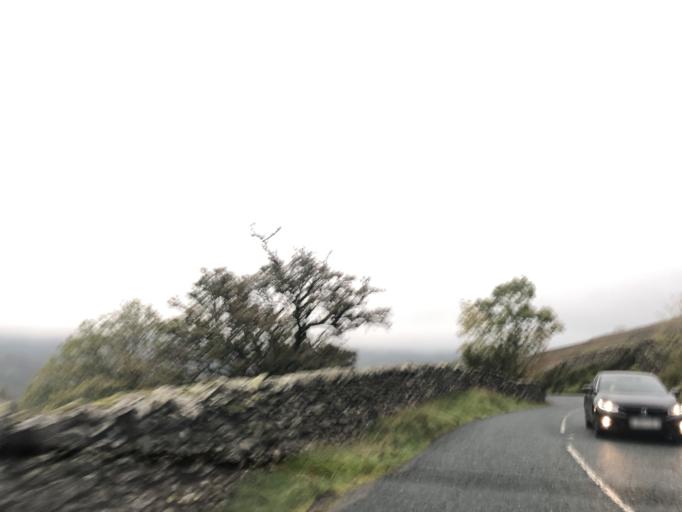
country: GB
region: England
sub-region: Cumbria
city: Ambleside
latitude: 54.4486
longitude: -2.9069
